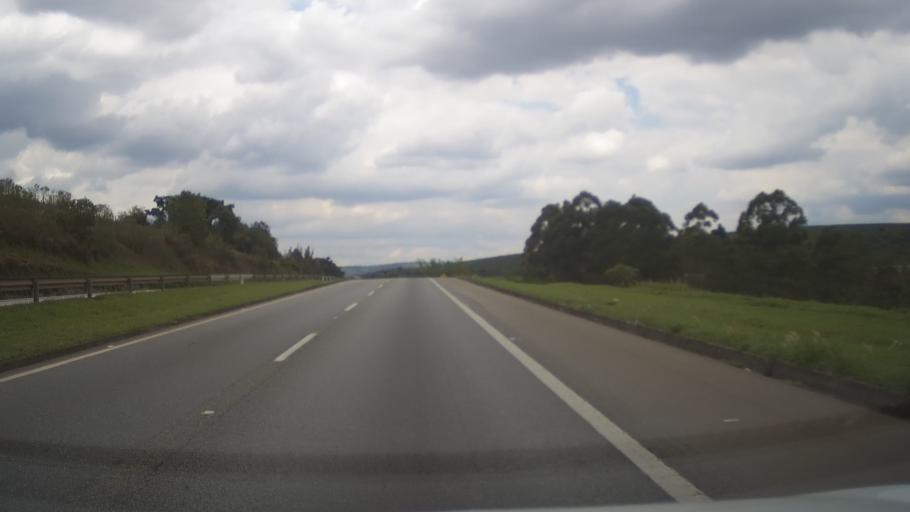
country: BR
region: Minas Gerais
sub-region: Tres Coracoes
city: Tres Coracoes
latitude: -21.5136
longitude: -45.2184
